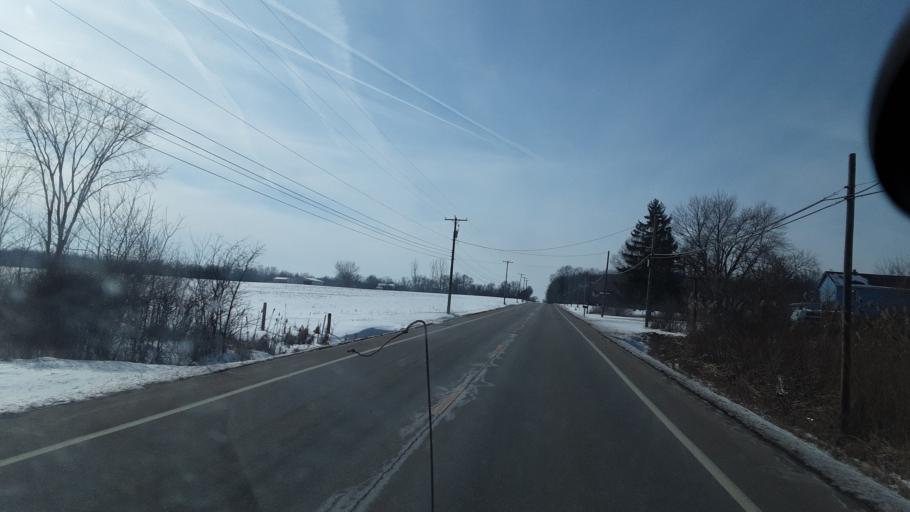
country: US
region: Ohio
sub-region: Mahoning County
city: Canfield
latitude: 41.0242
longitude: -80.8733
